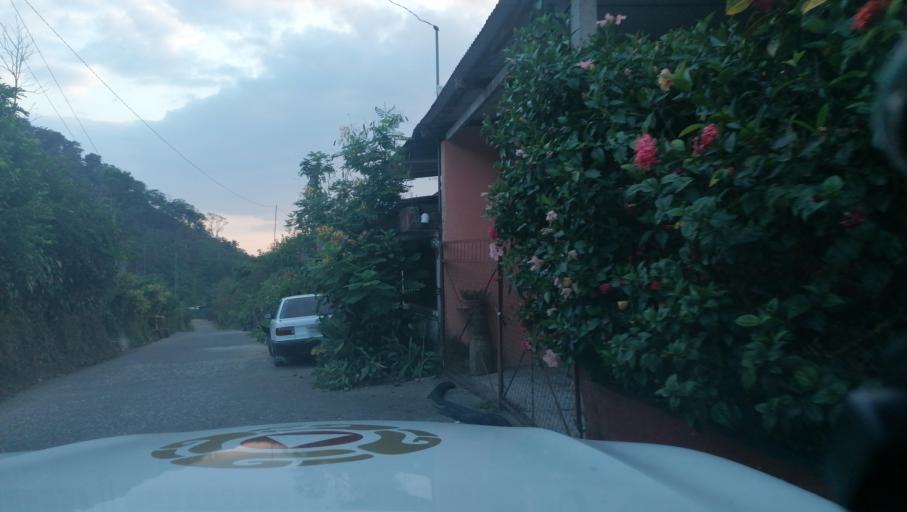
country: MX
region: Chiapas
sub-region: Cacahoatan
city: Benito Juarez
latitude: 15.0713
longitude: -92.2310
